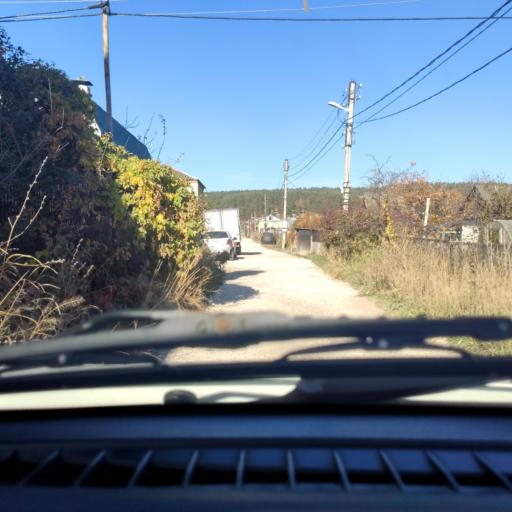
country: RU
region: Samara
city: Zhigulevsk
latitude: 53.4645
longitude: 49.5885
